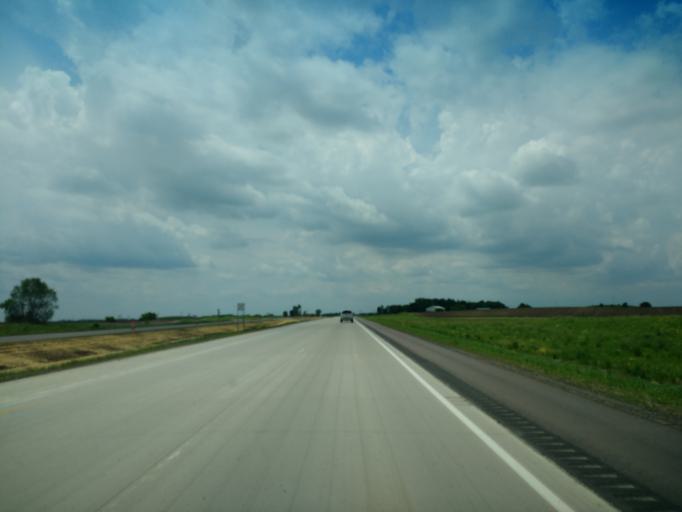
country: US
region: Minnesota
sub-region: Cottonwood County
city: Windom
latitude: 43.8962
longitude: -95.0776
